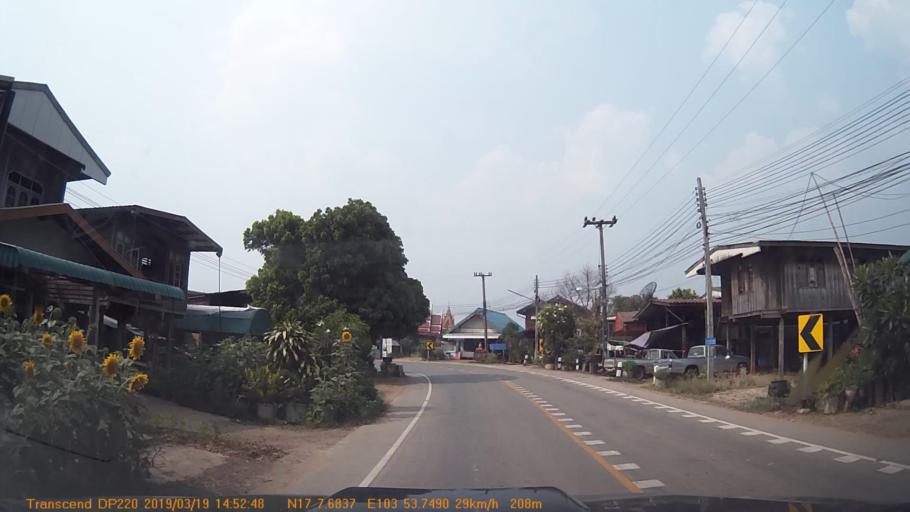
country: TH
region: Sakon Nakhon
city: Kut Bak
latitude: 17.1280
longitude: 103.8959
